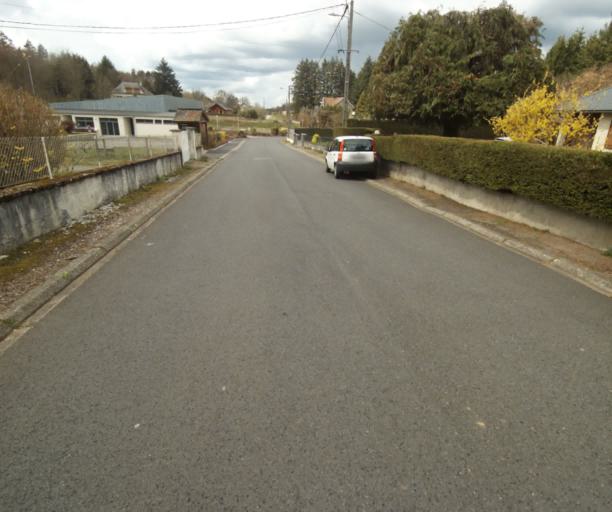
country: FR
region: Limousin
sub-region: Departement de la Correze
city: Correze
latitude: 45.3344
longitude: 1.9429
